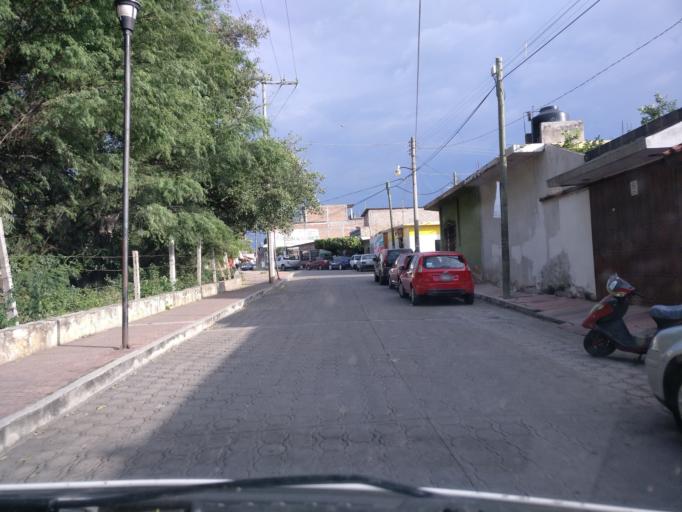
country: MX
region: Chiapas
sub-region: Chiapa de Corzo
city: Las Flechas
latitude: 16.7098
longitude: -93.0223
